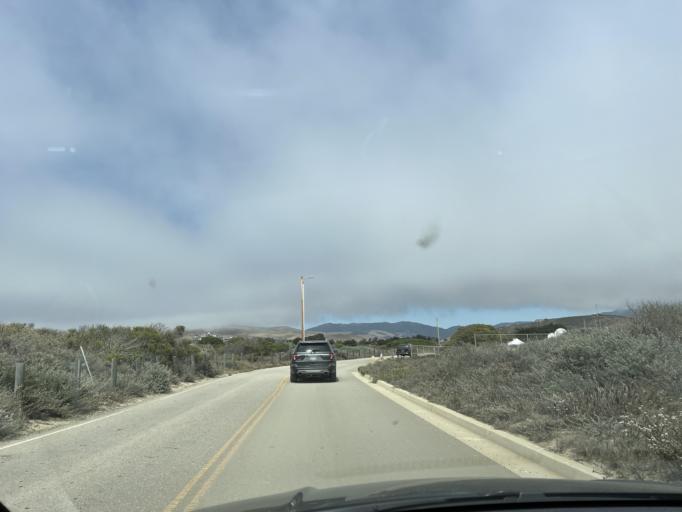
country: US
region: California
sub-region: San Luis Obispo County
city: Morro Bay
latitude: 35.3716
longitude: -120.8626
